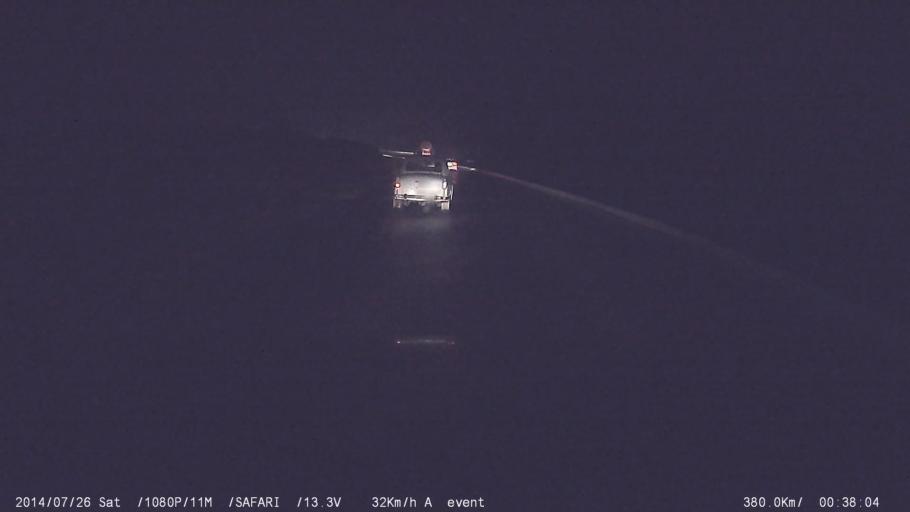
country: IN
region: Kerala
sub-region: Palakkad district
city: Chittur
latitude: 10.8254
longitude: 76.8169
